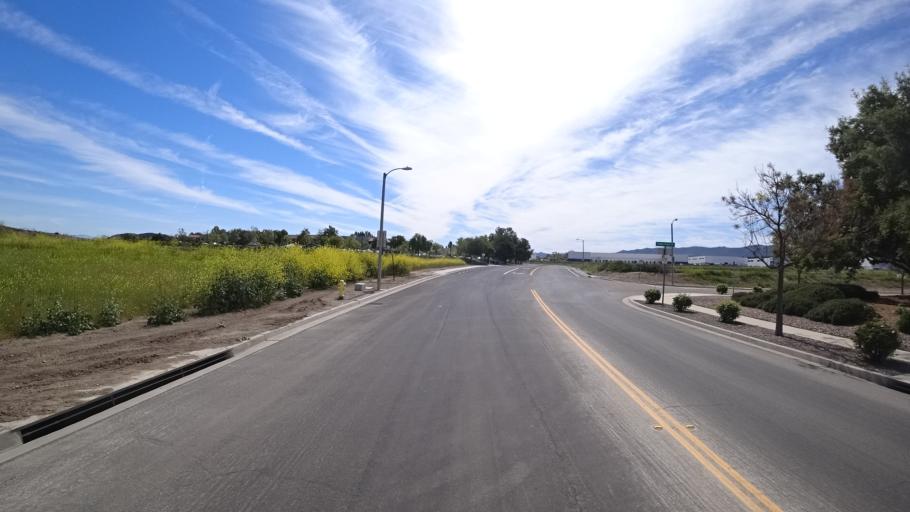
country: US
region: California
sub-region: Ventura County
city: Casa Conejo
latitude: 34.2063
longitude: -118.9332
